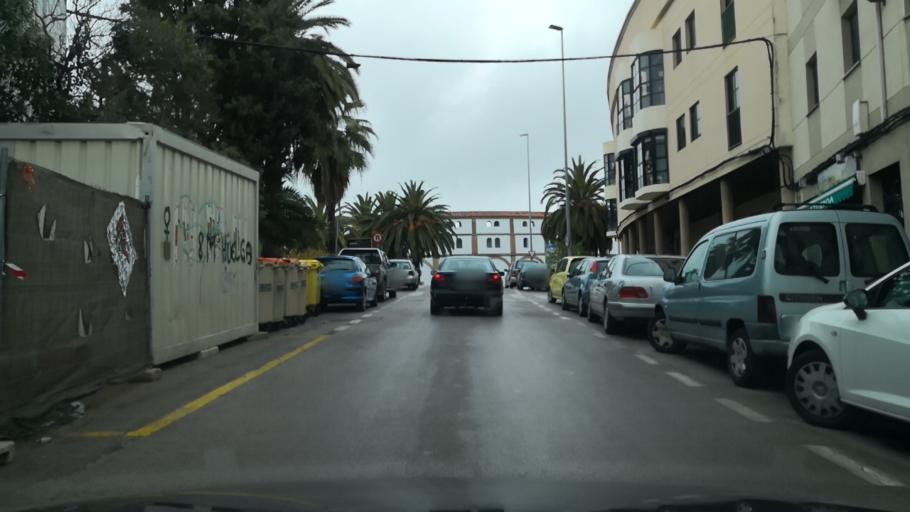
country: ES
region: Extremadura
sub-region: Provincia de Caceres
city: Caceres
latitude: 39.4793
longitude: -6.3748
